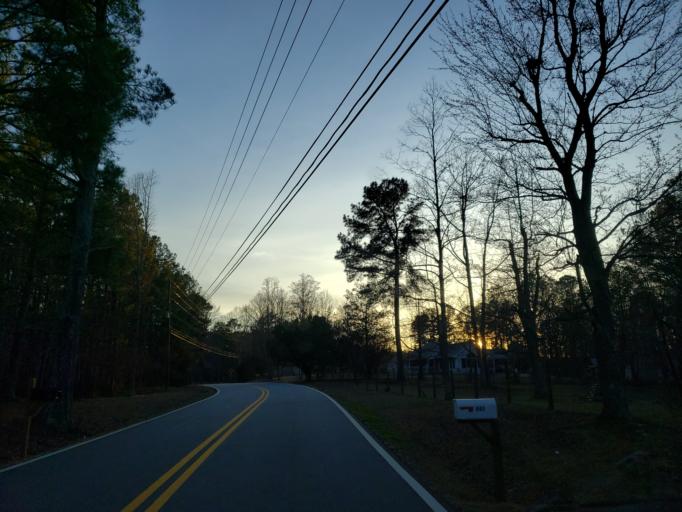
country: US
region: Georgia
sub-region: Cobb County
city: Acworth
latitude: 34.0117
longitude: -84.7442
